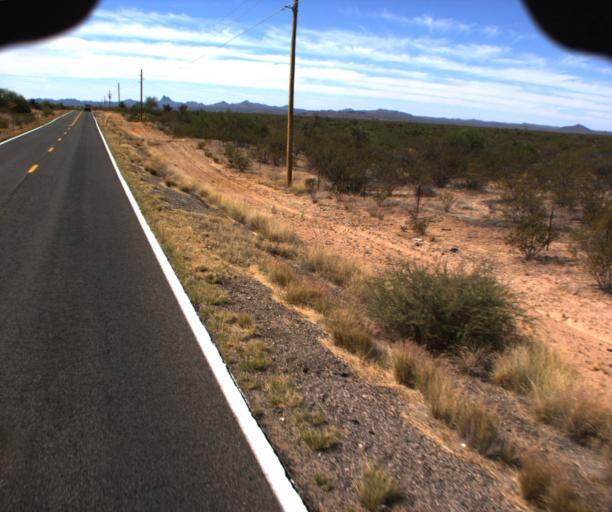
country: US
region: Arizona
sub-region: Yavapai County
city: Congress
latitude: 34.0809
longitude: -112.8245
